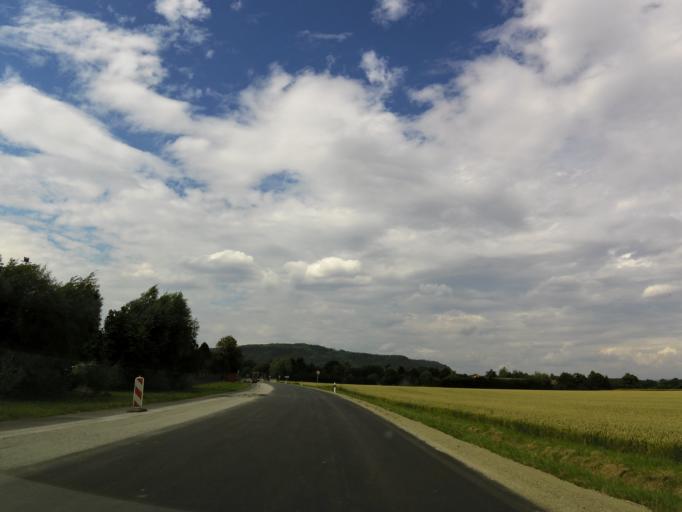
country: DE
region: North Rhine-Westphalia
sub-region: Regierungsbezirk Detmold
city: Hoexter
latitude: 51.7659
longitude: 9.3869
